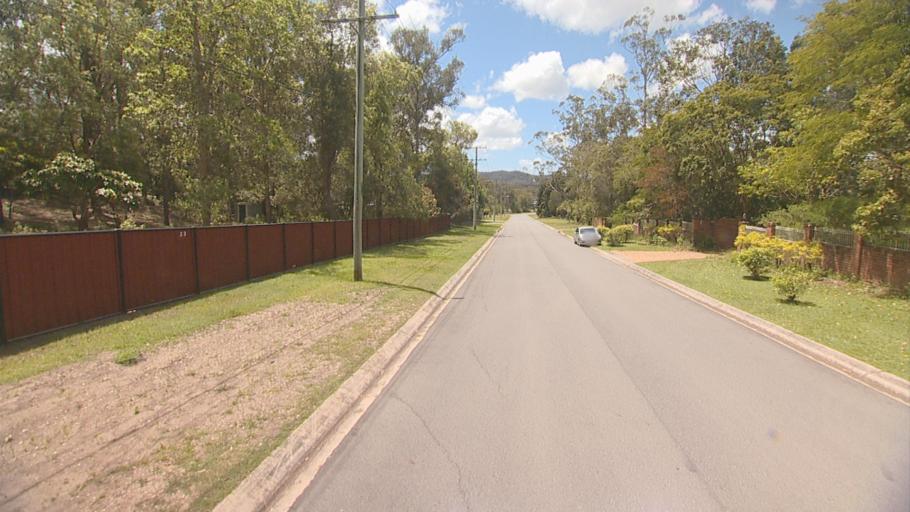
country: AU
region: Queensland
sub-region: Logan
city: Beenleigh
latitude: -27.6690
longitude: 153.2167
